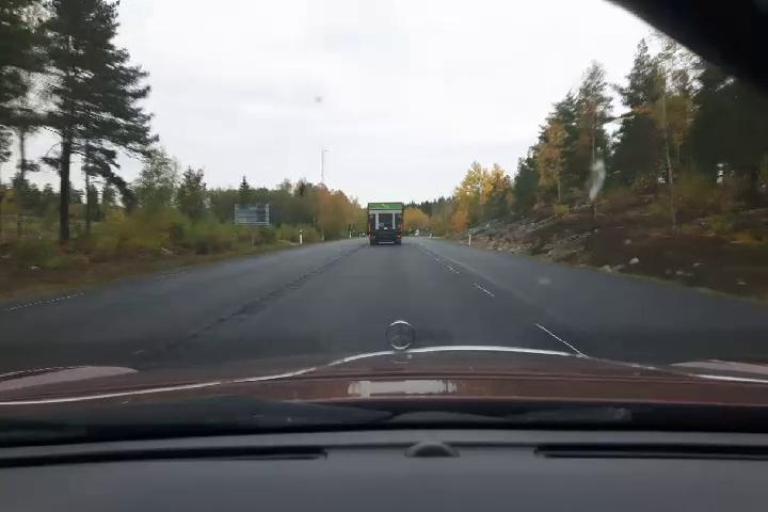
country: SE
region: Soedermanland
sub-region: Strangnas Kommun
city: Strangnas
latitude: 59.4107
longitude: 17.0204
